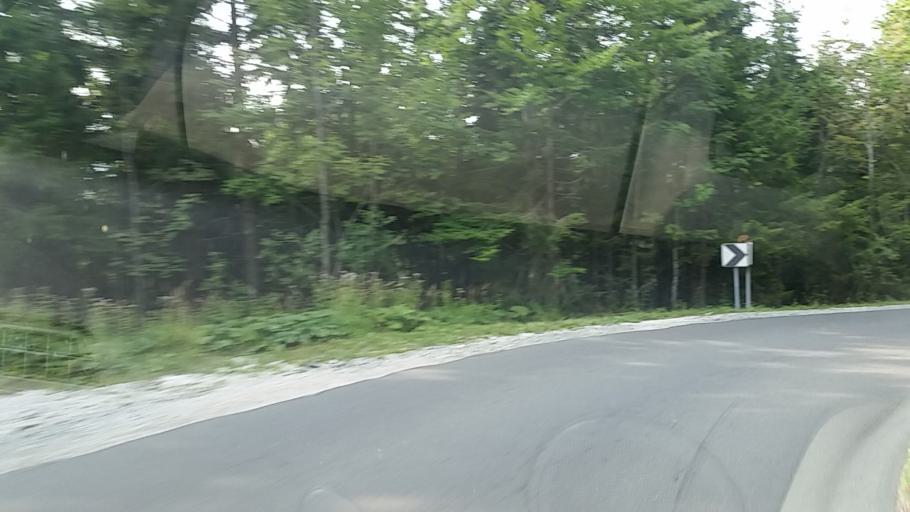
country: SI
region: Bohinj
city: Bohinjska Bistrica
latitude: 46.2696
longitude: 14.0169
